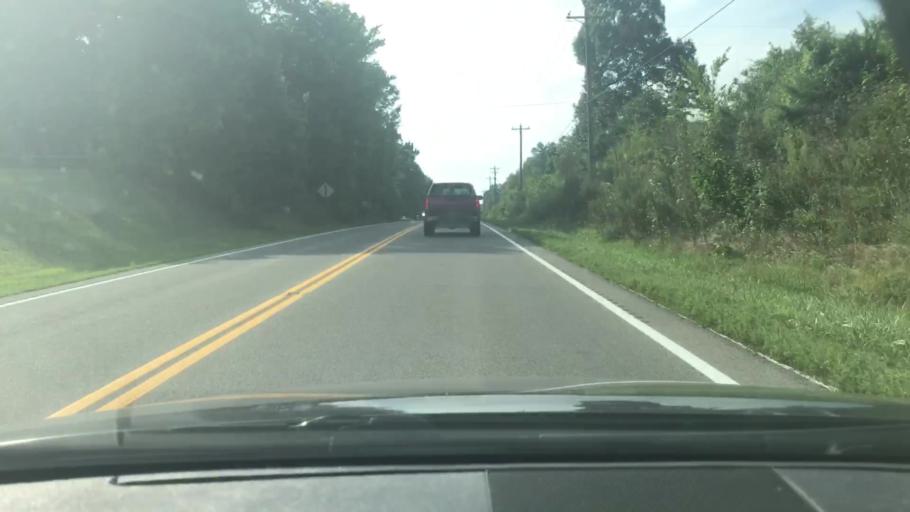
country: US
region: Tennessee
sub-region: Williamson County
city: Fairview
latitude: 36.0096
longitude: -87.1450
